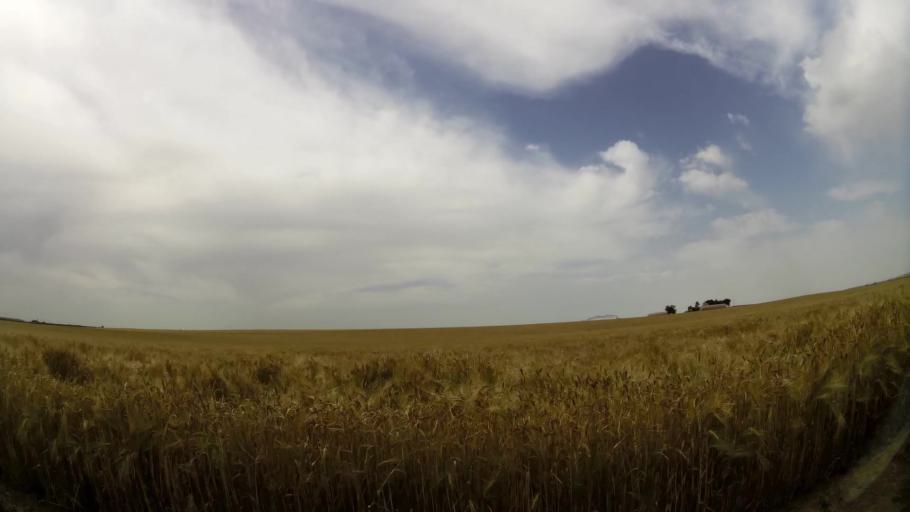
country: MA
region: Rabat-Sale-Zemmour-Zaer
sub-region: Khemisset
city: Tiflet
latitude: 33.7581
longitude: -6.2182
